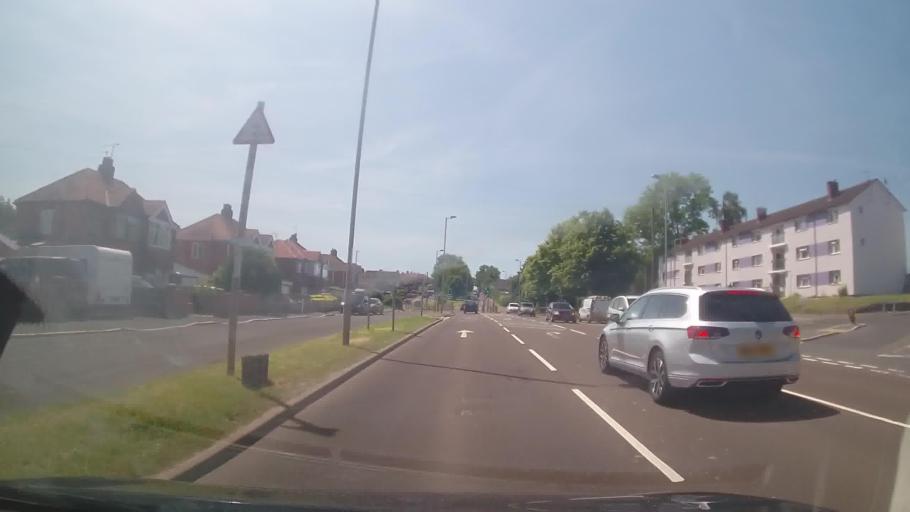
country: GB
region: England
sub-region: Herefordshire
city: Hereford
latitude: 52.0404
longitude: -2.7208
